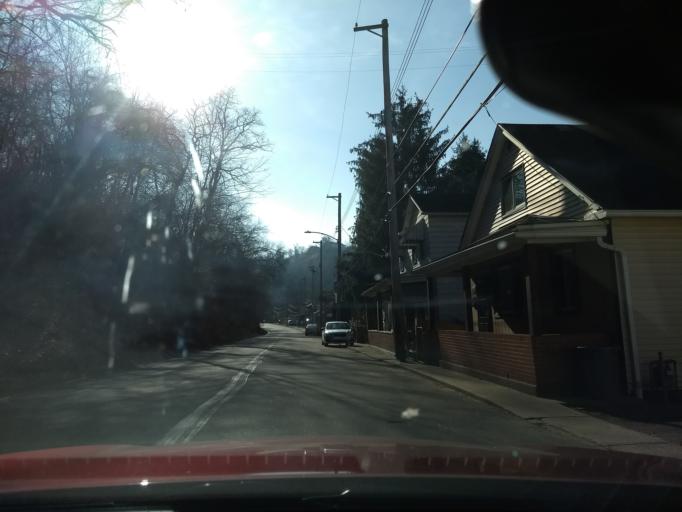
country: US
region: Pennsylvania
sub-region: Allegheny County
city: Whitaker
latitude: 40.4055
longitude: -79.8964
